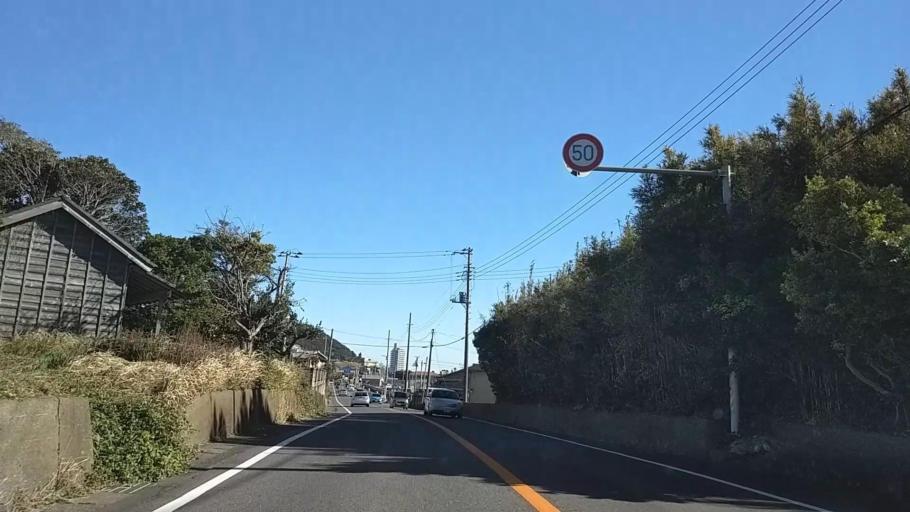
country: JP
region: Chiba
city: Kawaguchi
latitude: 35.0596
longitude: 140.0570
